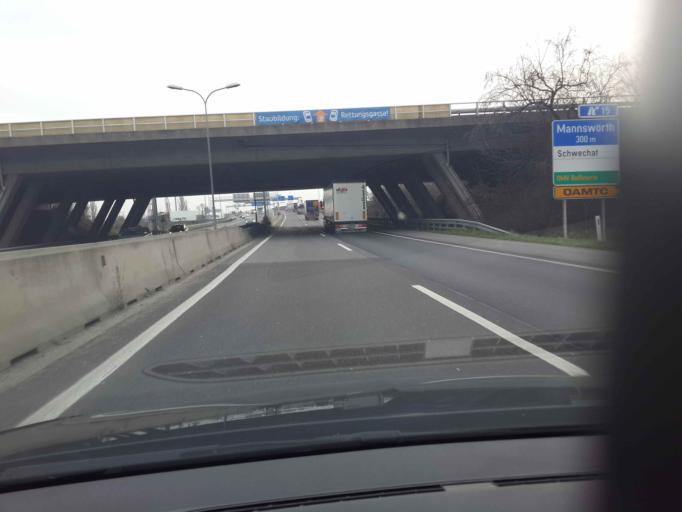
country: AT
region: Lower Austria
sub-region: Politischer Bezirk Wien-Umgebung
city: Schwechat
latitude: 48.1513
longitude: 16.4897
